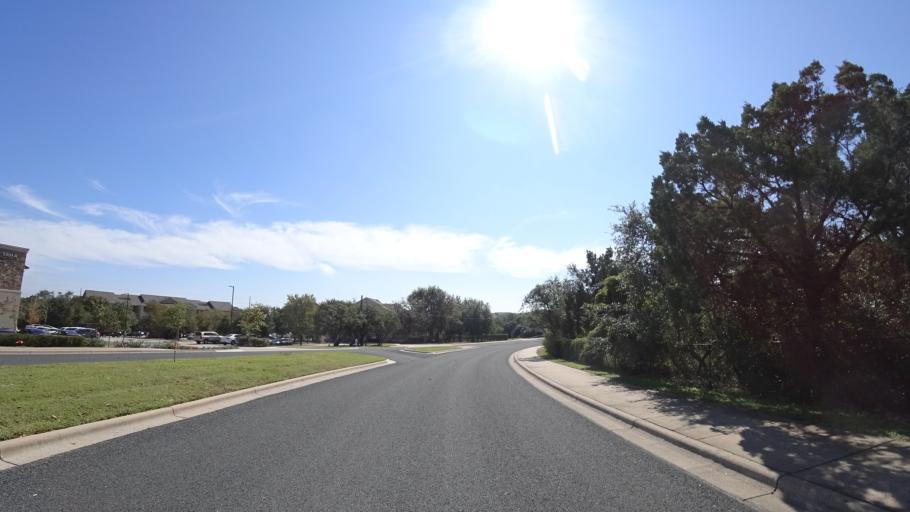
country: US
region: Texas
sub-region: Travis County
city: Shady Hollow
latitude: 30.2082
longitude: -97.8643
